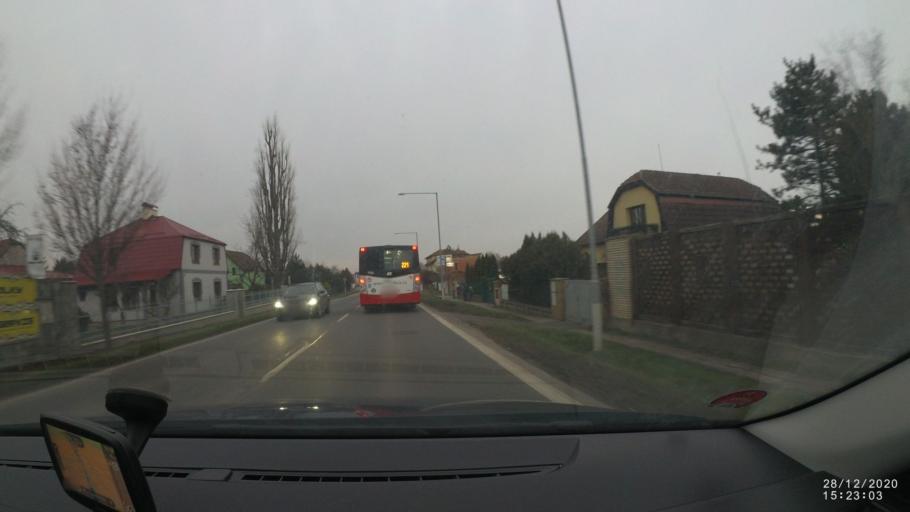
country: CZ
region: Central Bohemia
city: Sestajovice
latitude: 50.0777
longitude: 14.6522
